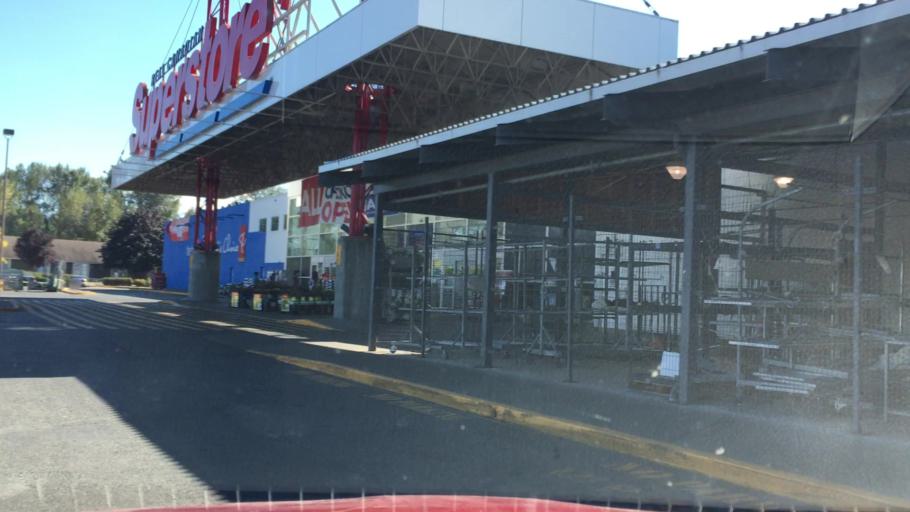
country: CA
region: British Columbia
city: Duncan
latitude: 48.7748
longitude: -123.7034
